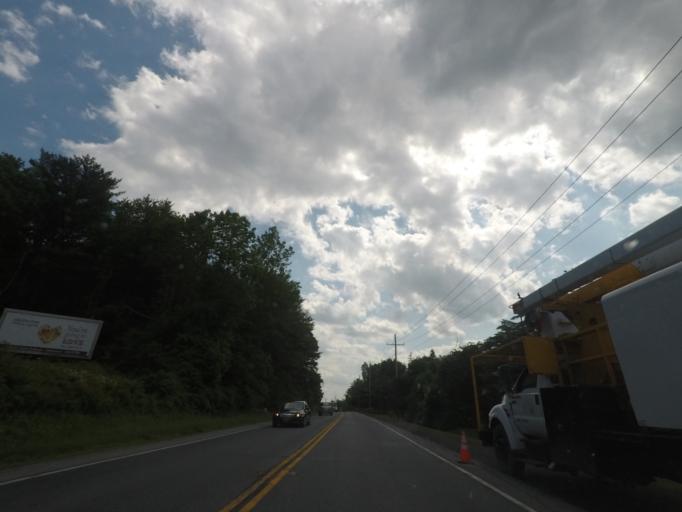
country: US
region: New York
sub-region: Dutchess County
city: Pleasant Valley
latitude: 41.7723
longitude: -73.7725
